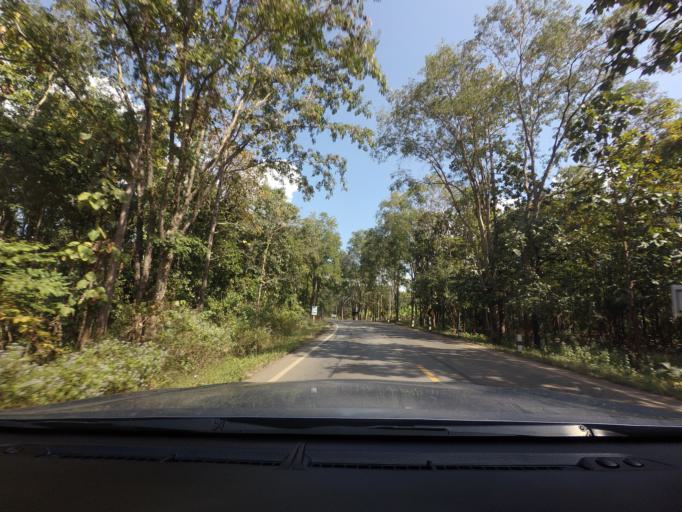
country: TH
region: Chiang Mai
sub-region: Amphoe Chiang Dao
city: Chiang Dao
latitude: 19.4913
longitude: 99.0312
